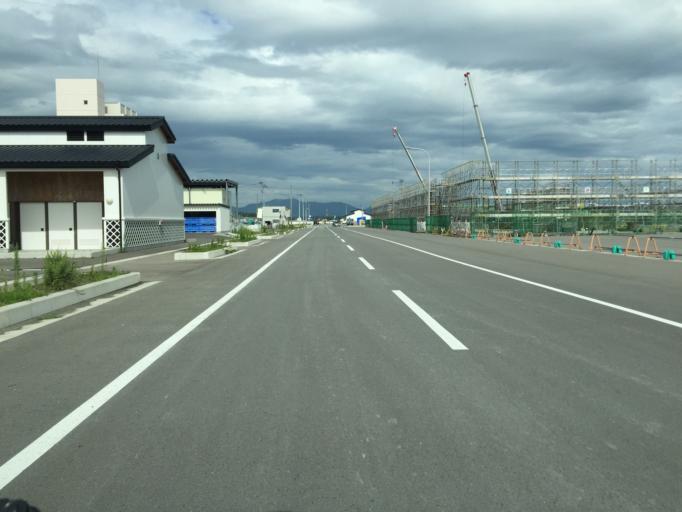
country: JP
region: Miyagi
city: Marumori
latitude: 37.8275
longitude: 140.9740
